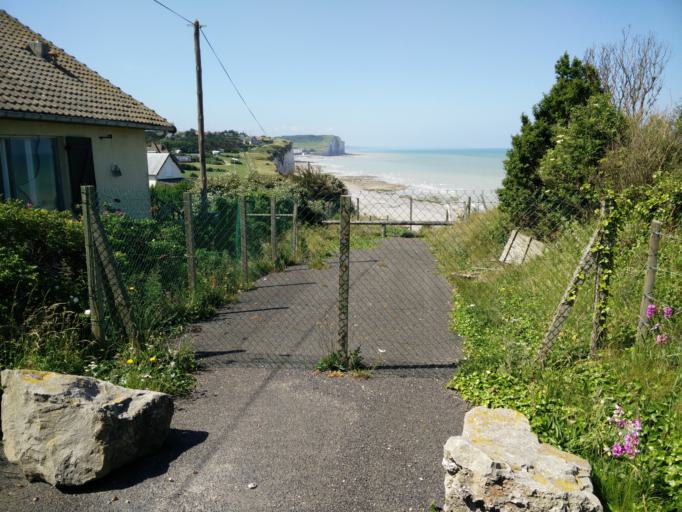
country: FR
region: Haute-Normandie
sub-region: Departement de la Seine-Maritime
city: Criel-sur-Mer
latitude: 50.0464
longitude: 1.3318
